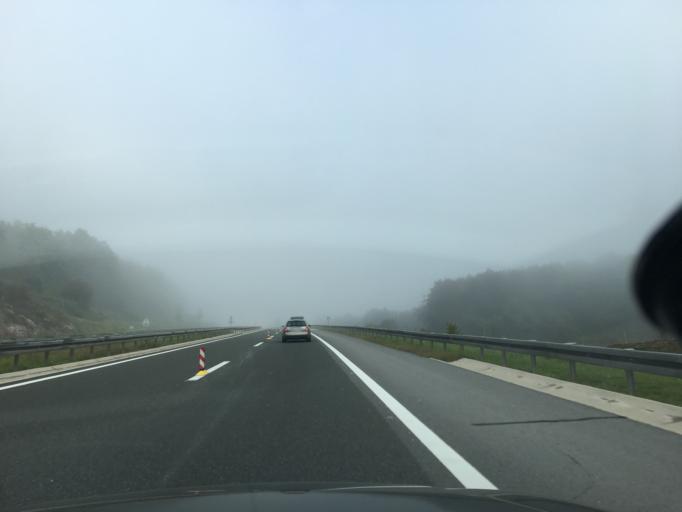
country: HR
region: Licko-Senjska
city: Otocac
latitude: 44.8774
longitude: 15.2053
